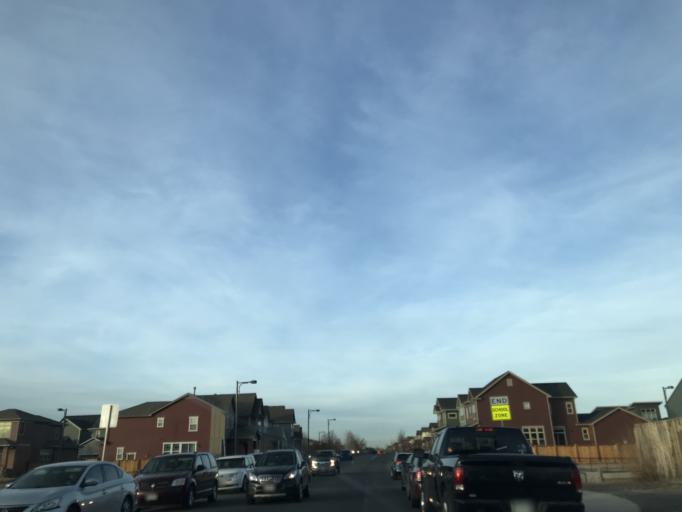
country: US
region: Colorado
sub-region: Adams County
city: Aurora
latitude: 39.7535
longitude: -104.8646
